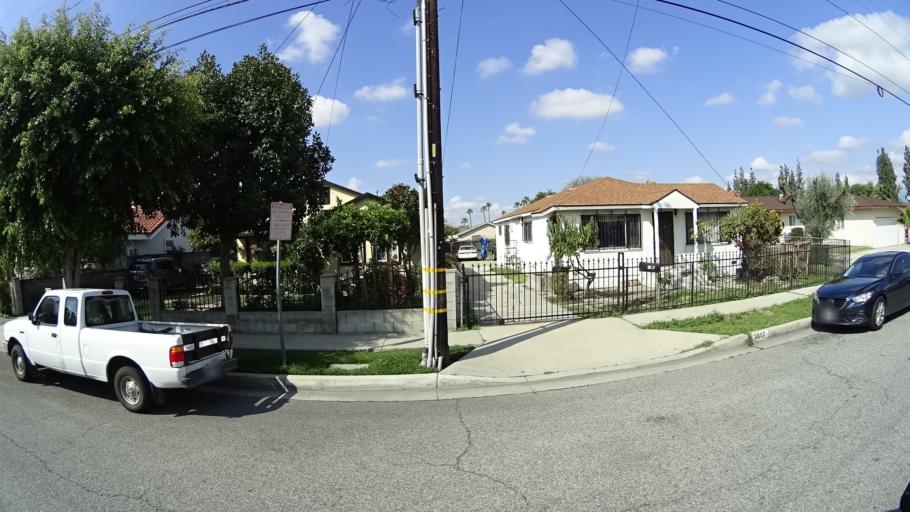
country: US
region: California
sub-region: Los Angeles County
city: Baldwin Park
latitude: 34.0806
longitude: -117.9784
